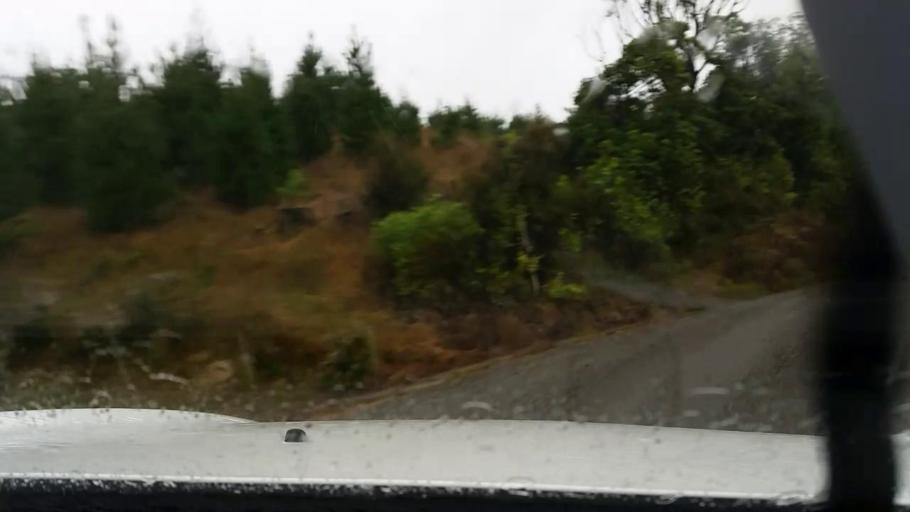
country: NZ
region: Wellington
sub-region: Masterton District
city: Masterton
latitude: -41.2057
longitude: 175.8145
